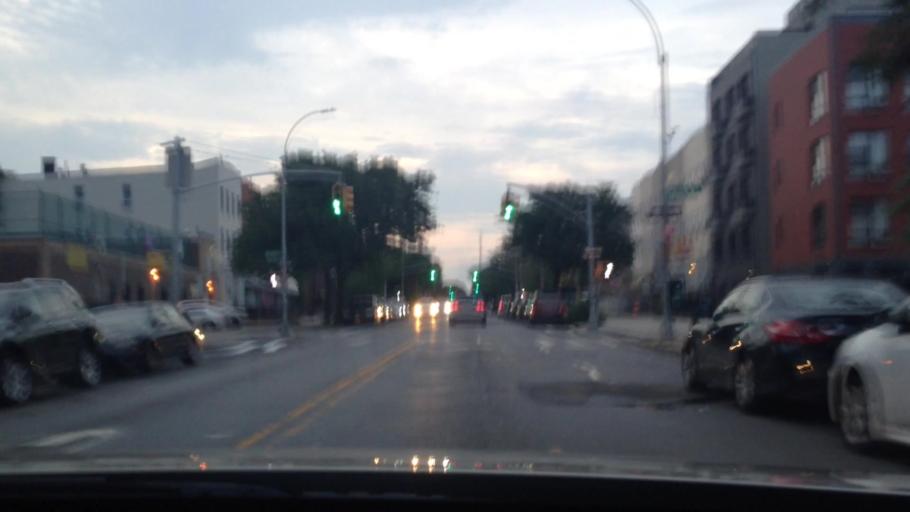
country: US
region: New York
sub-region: Kings County
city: East New York
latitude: 40.6856
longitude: -73.9112
